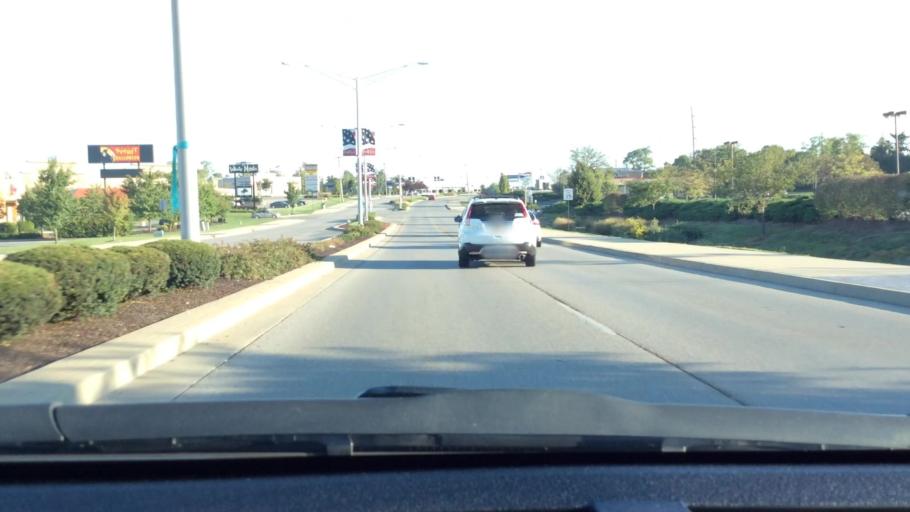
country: US
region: Kentucky
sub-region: Boone County
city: Florence
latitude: 38.9994
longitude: -84.6535
